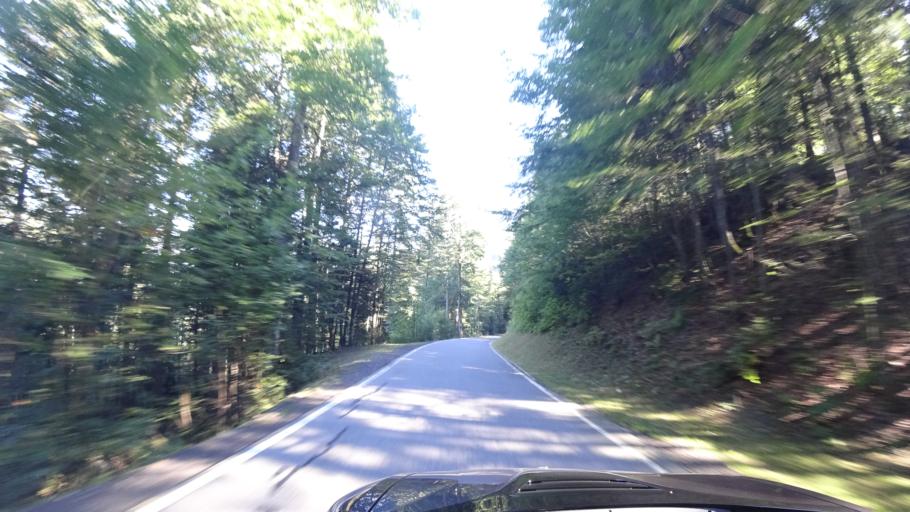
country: CH
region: Obwalden
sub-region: Obwalden
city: Lungern
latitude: 46.8274
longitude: 8.1215
